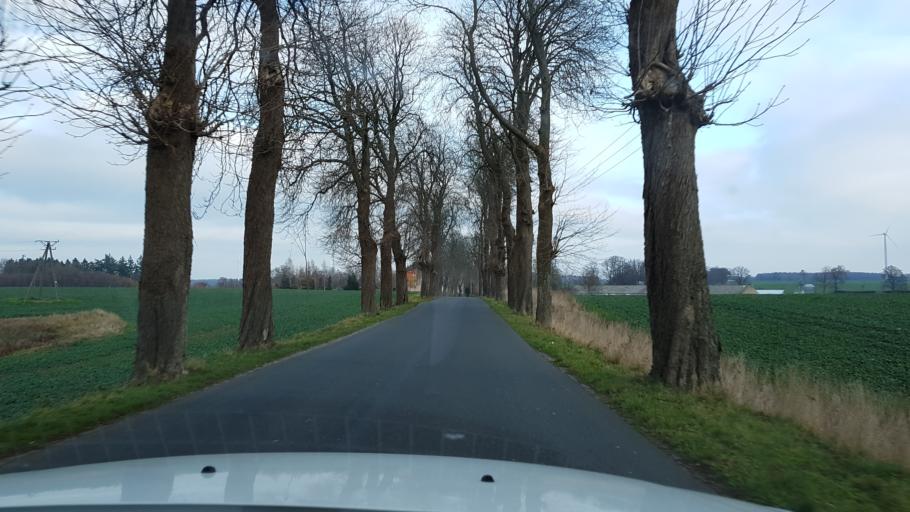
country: PL
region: West Pomeranian Voivodeship
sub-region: Powiat kolobrzeski
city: Goscino
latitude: 54.0556
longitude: 15.6785
